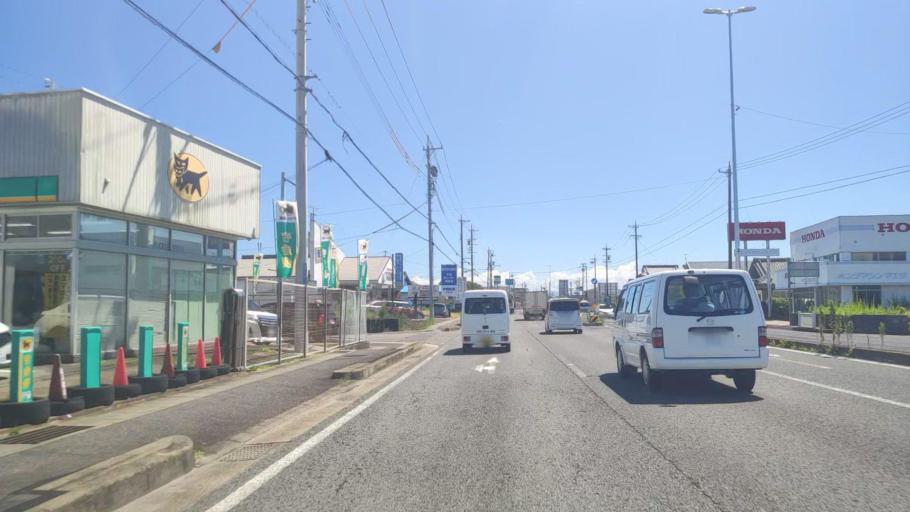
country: JP
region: Mie
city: Kawage
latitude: 34.8146
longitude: 136.5698
